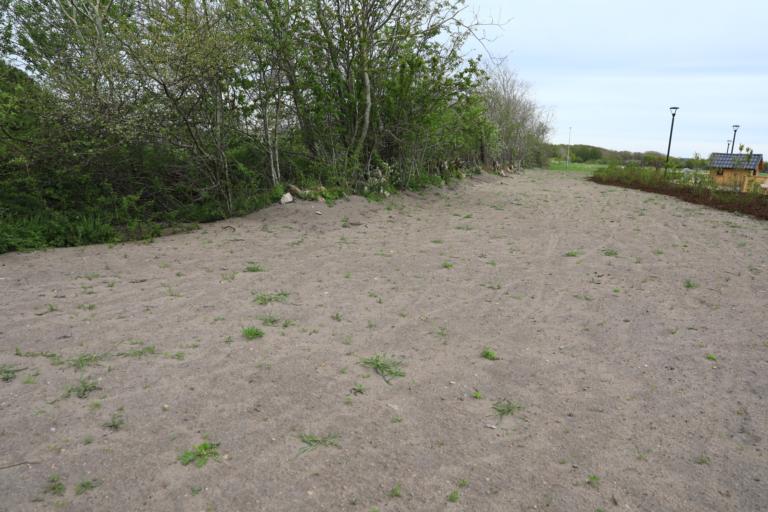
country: SE
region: Halland
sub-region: Varbergs Kommun
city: Varberg
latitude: 57.1485
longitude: 12.2347
